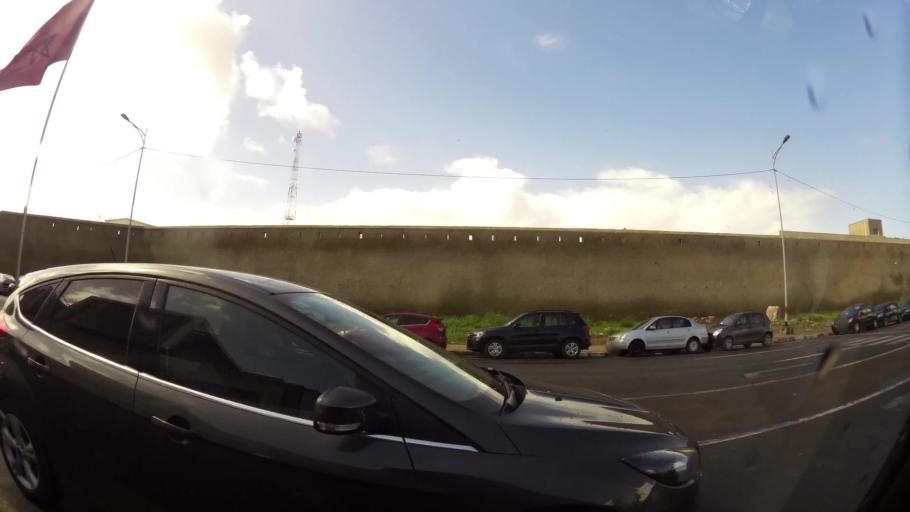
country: MA
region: Grand Casablanca
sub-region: Casablanca
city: Casablanca
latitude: 33.6070
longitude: -7.6224
